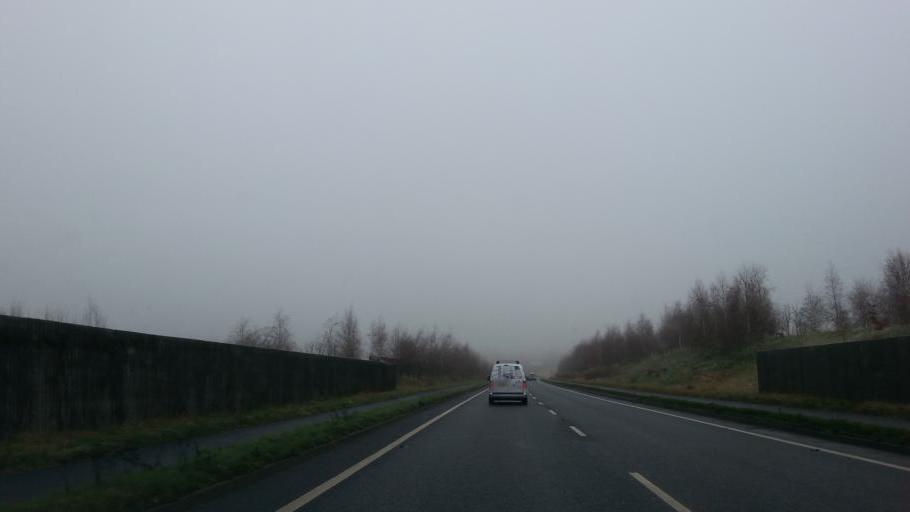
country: GB
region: England
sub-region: Cheshire East
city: Alderley Edge
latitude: 53.3028
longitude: -2.2482
